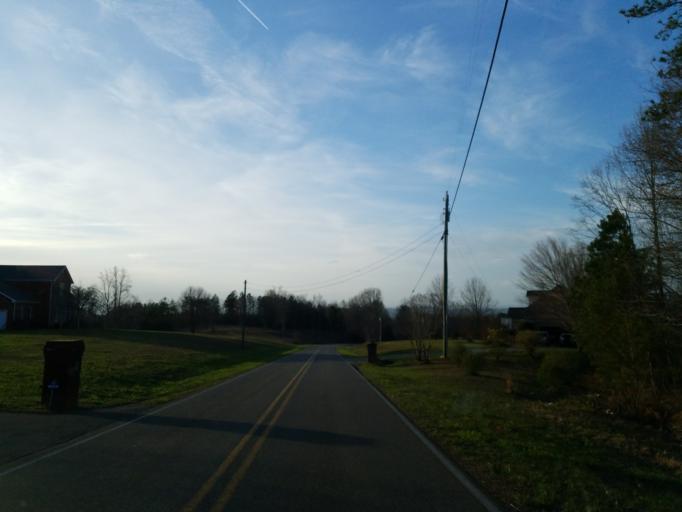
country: US
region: Georgia
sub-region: Pickens County
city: Jasper
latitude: 34.4975
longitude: -84.5189
